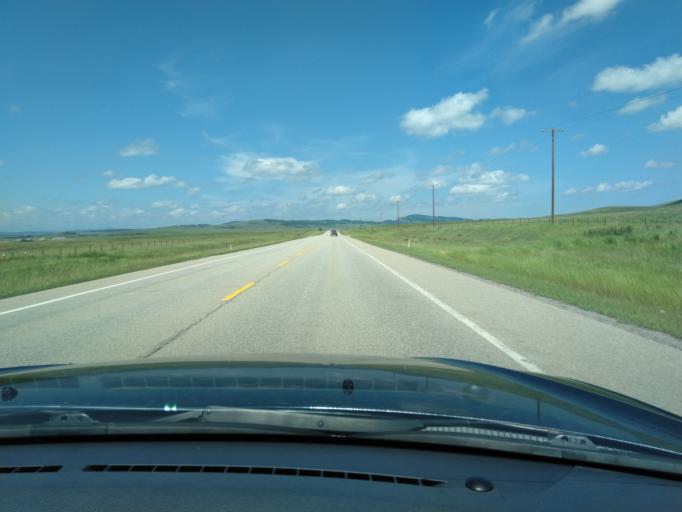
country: CA
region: Alberta
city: Cochrane
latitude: 51.2233
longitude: -114.5491
